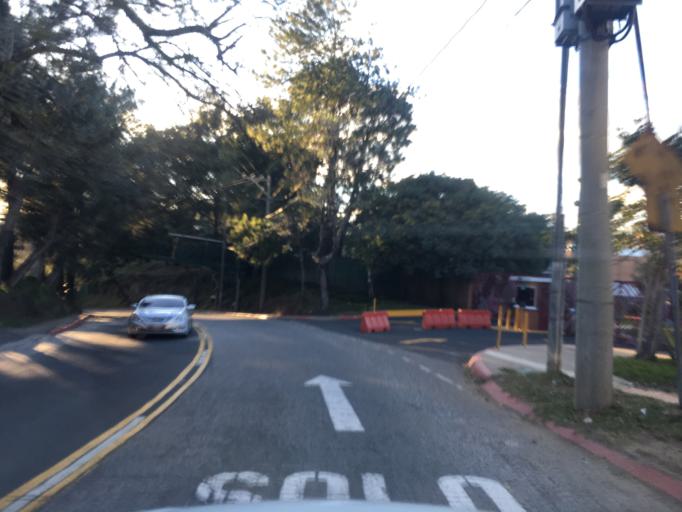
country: GT
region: Guatemala
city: Santa Catarina Pinula
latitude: 14.6048
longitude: -90.4910
